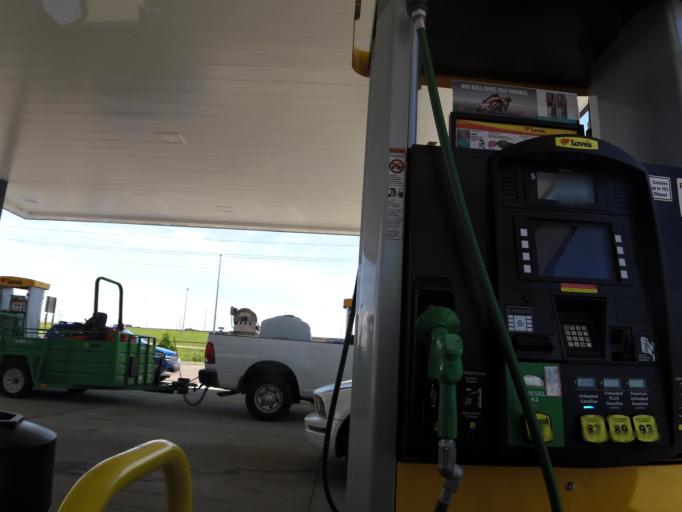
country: US
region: Tennessee
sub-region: Dyer County
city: Dyersburg
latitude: 36.0712
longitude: -89.3960
